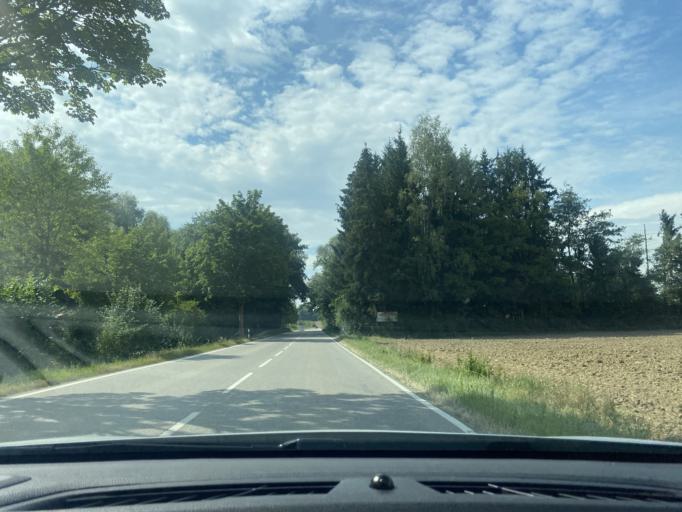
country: DE
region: Bavaria
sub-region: Upper Bavaria
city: Zolling
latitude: 48.4543
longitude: 11.7788
